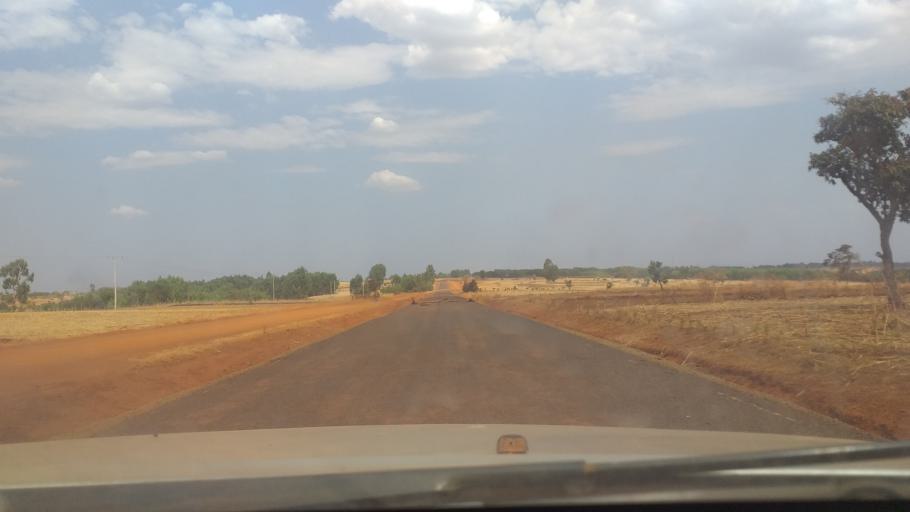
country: ET
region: Binshangul Gumuz
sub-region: Asosa
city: Asosa
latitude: 10.0787
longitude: 34.6438
